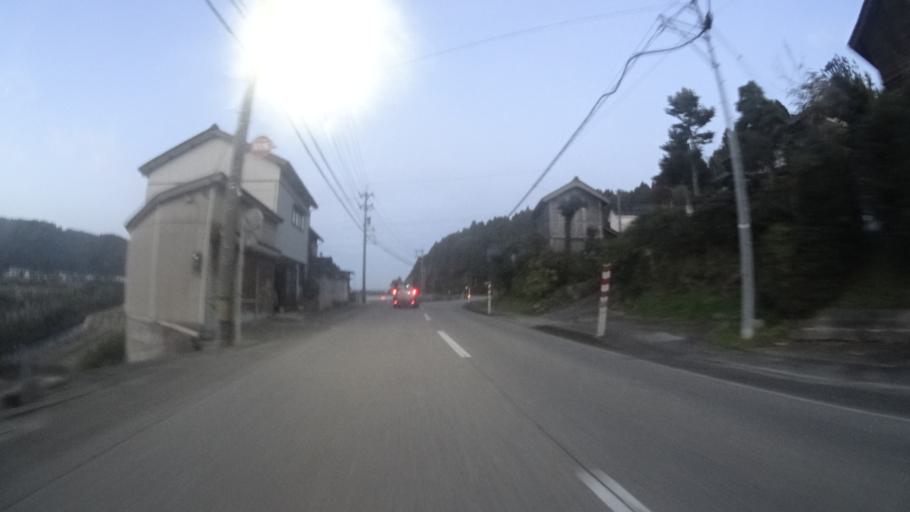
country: JP
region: Ishikawa
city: Nanao
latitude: 37.3726
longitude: 136.8776
